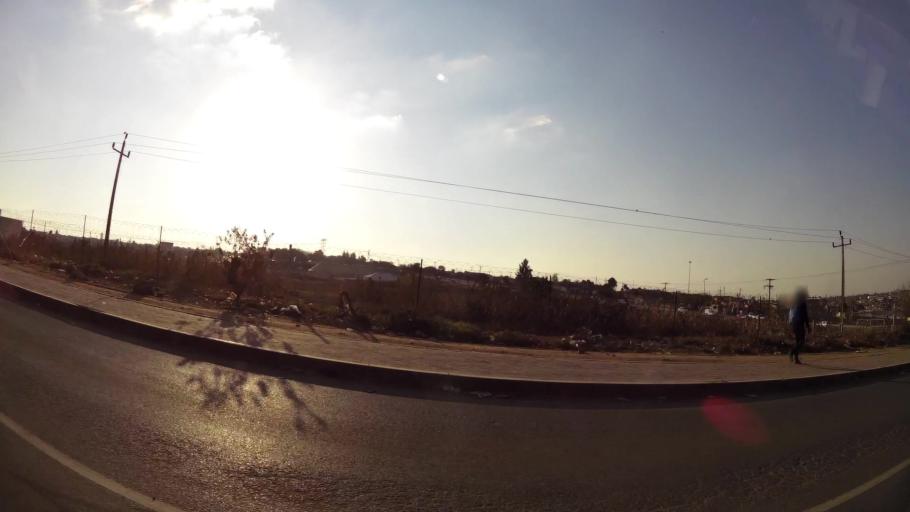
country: ZA
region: Gauteng
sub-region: Ekurhuleni Metropolitan Municipality
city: Tembisa
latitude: -26.0017
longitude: 28.1922
